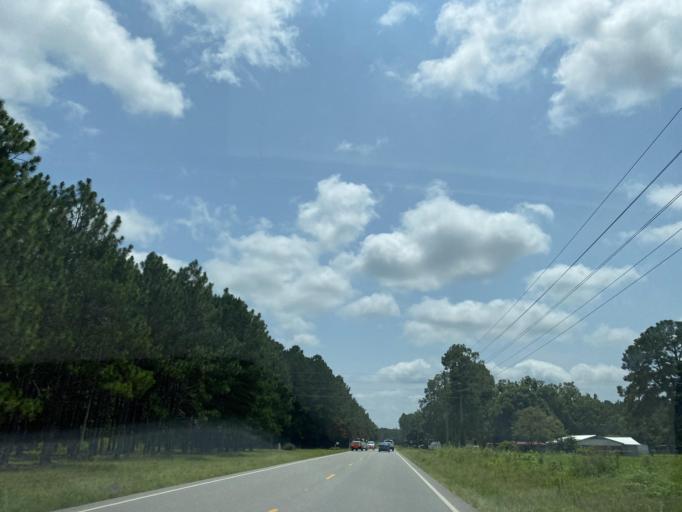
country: US
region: Georgia
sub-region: Jeff Davis County
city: Hazlehurst
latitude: 31.8012
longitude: -82.5656
